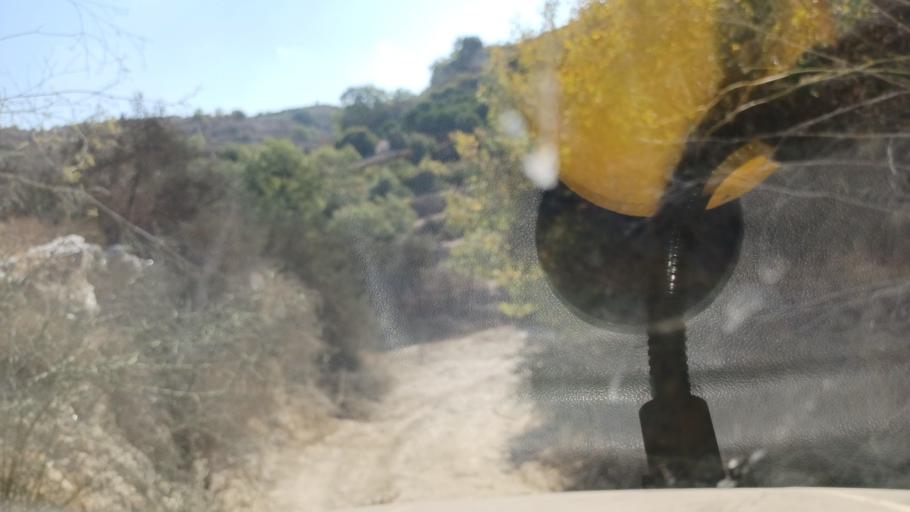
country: CY
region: Pafos
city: Pegeia
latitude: 34.9211
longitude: 32.4601
